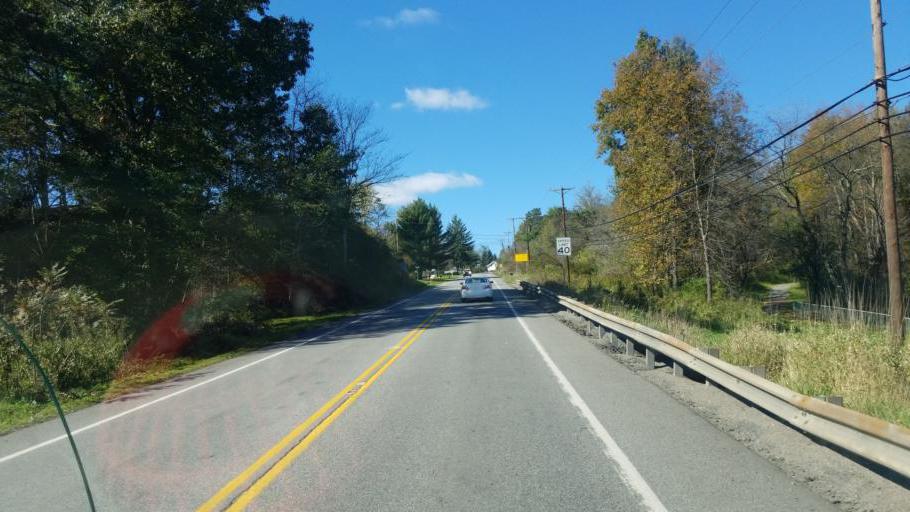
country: US
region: Pennsylvania
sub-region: Somerset County
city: Boswell
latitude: 40.1481
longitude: -79.0439
